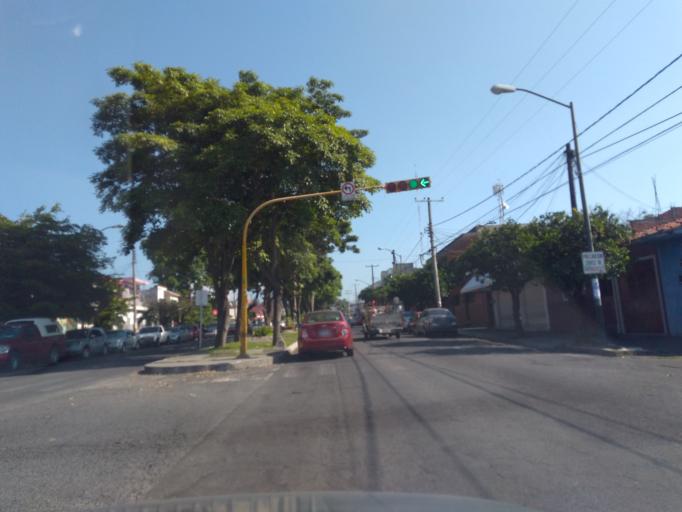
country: MX
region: Colima
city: Colima
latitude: 19.2511
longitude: -103.7315
